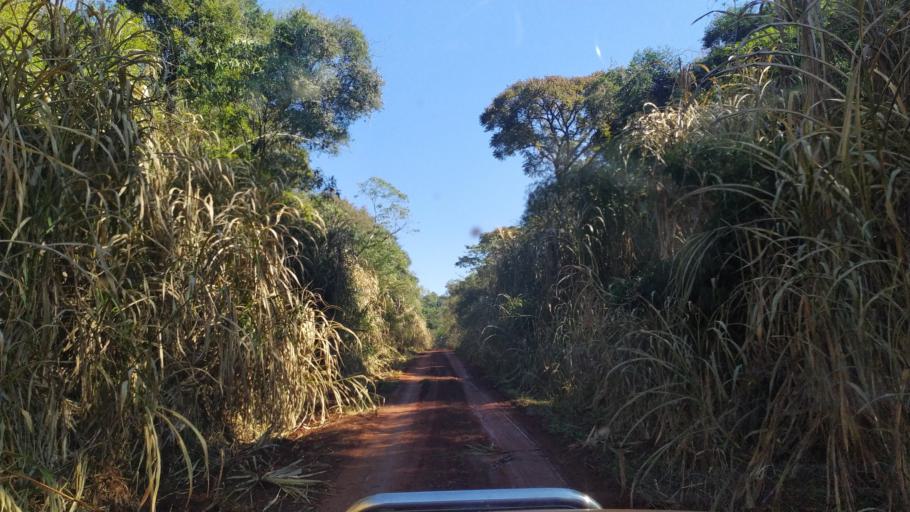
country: AR
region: Misiones
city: El Alcazar
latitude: -26.7520
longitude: -54.6056
